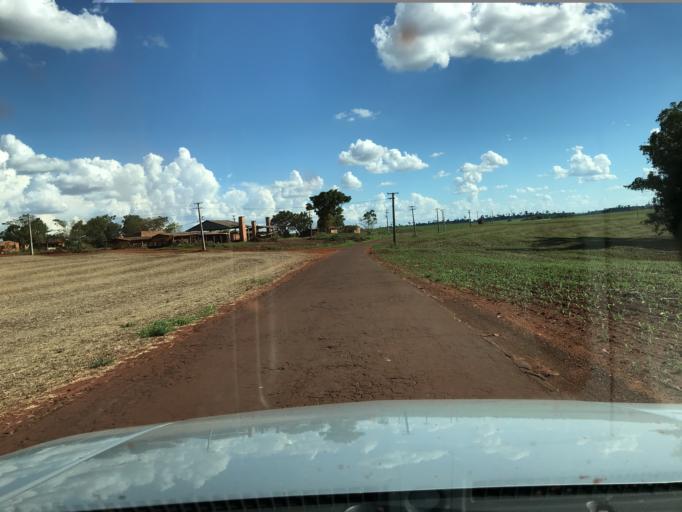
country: BR
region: Parana
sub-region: Palotina
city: Palotina
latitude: -24.2467
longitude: -53.7923
